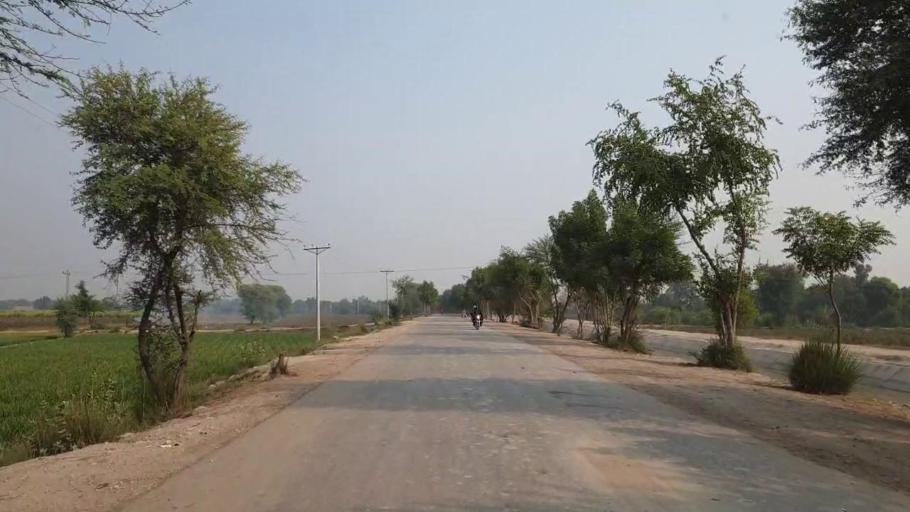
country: PK
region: Sindh
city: Bhan
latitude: 26.5873
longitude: 67.7299
